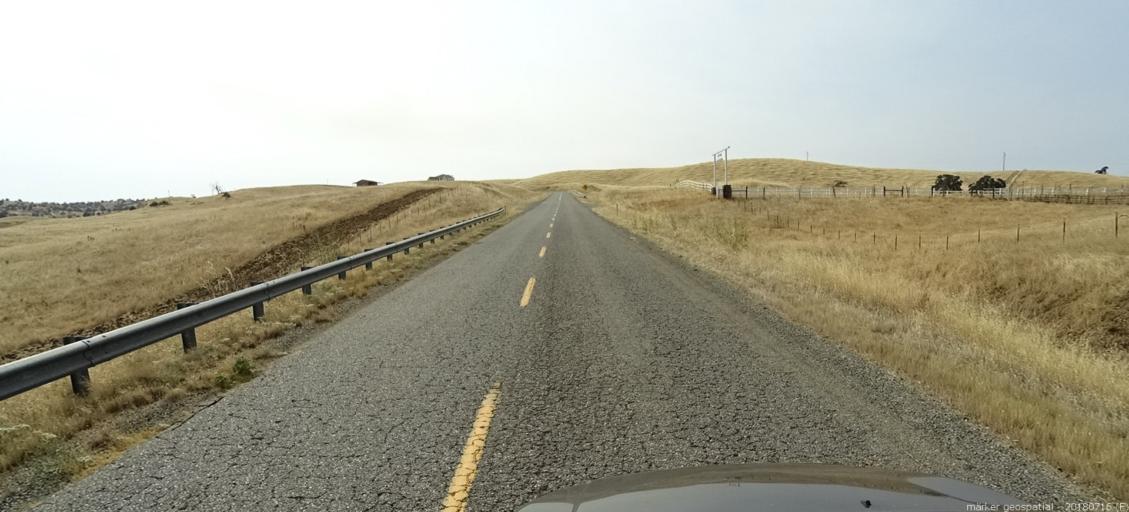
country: US
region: California
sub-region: Madera County
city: Bonadelle Ranchos-Madera Ranchos
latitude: 37.1020
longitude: -119.8850
